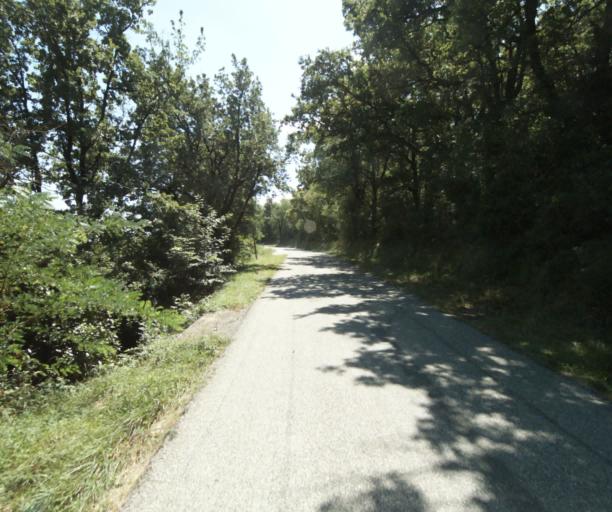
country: FR
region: Midi-Pyrenees
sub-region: Departement de la Haute-Garonne
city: Saint-Felix-Lauragais
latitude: 43.4793
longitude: 1.8700
